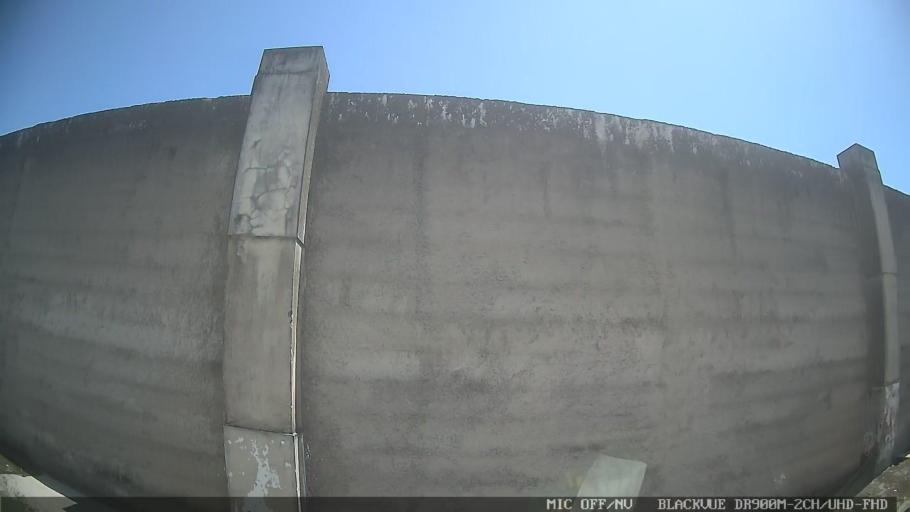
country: BR
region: Sao Paulo
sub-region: Sao Sebastiao
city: Sao Sebastiao
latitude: -23.7102
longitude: -45.4305
